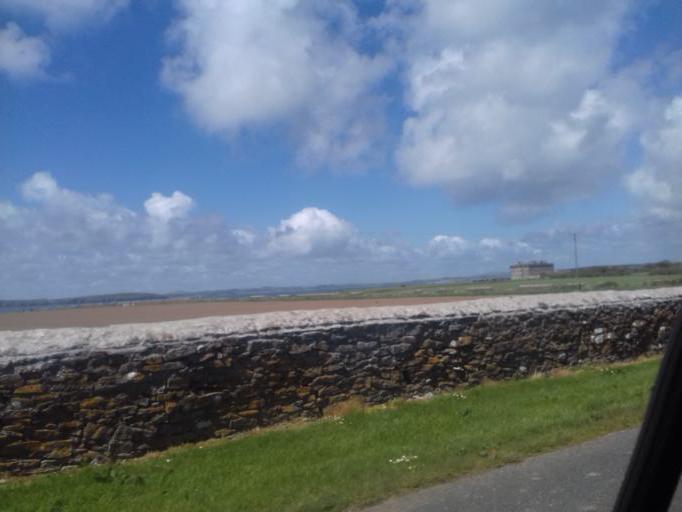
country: IE
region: Munster
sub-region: Waterford
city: Dunmore East
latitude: 52.1433
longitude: -6.9104
